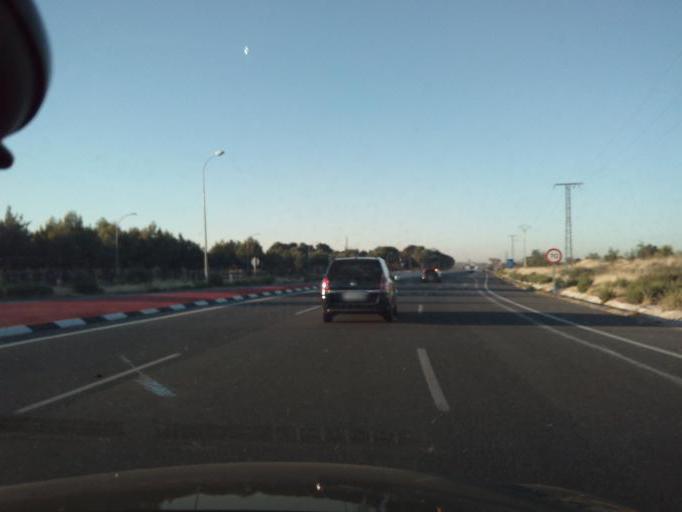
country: ES
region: Madrid
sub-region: Provincia de Madrid
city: Torrejon de Ardoz
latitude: 40.4919
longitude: -3.4787
